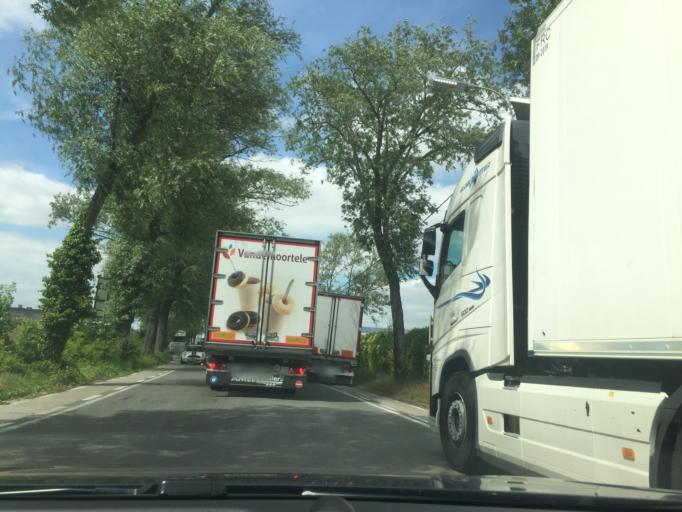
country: BE
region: Flanders
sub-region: Provincie West-Vlaanderen
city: Kortrijk
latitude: 50.8542
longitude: 3.2513
